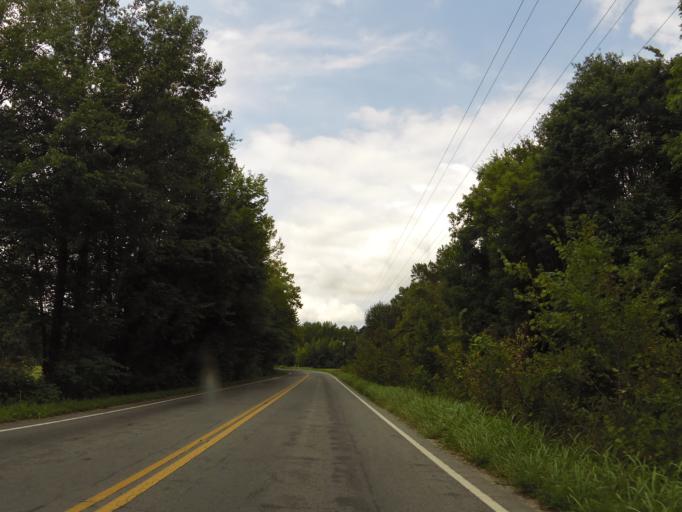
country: US
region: Tennessee
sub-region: Perry County
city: Linden
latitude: 35.6223
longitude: -87.9445
